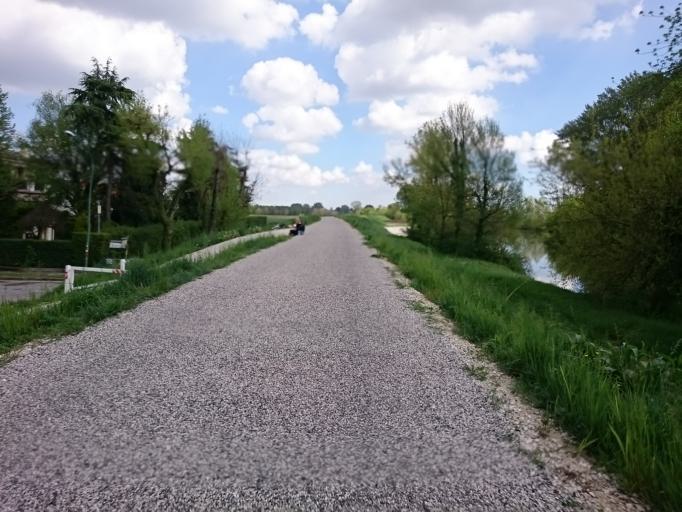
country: IT
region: Veneto
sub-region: Provincia di Padova
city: Tencarola
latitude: 45.3877
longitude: 11.8157
